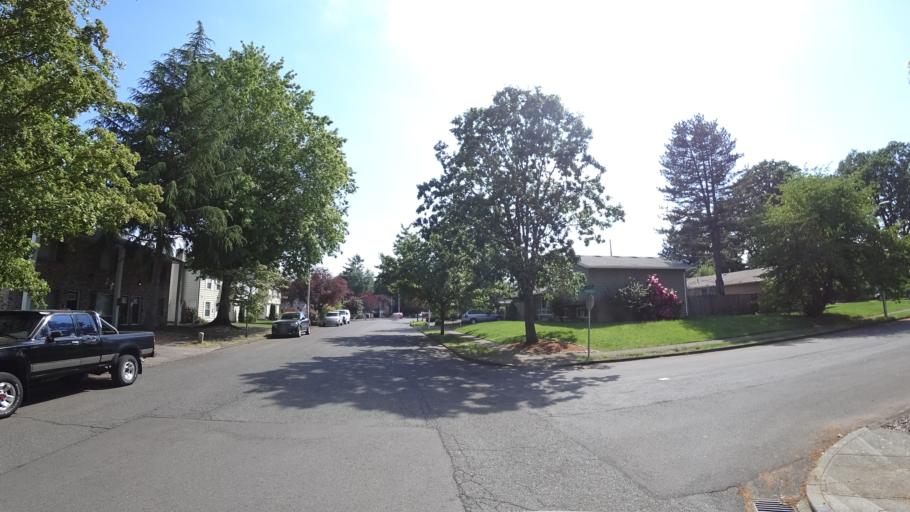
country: US
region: Oregon
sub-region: Washington County
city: Beaverton
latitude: 45.4643
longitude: -122.7925
